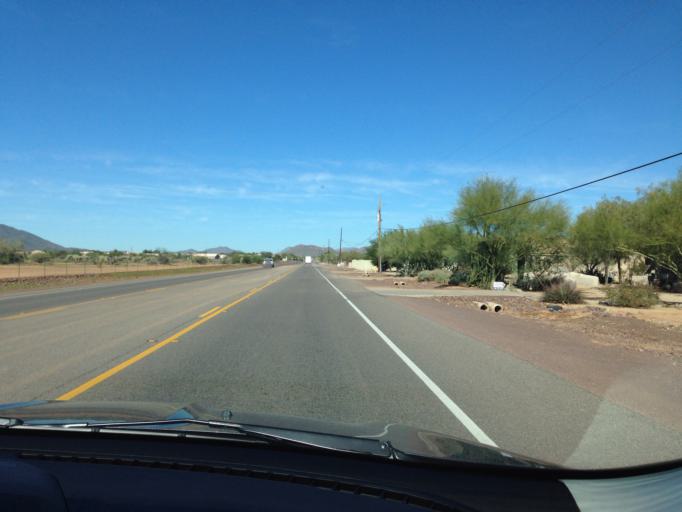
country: US
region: Arizona
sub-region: Maricopa County
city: Anthem
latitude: 33.8228
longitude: -112.0654
